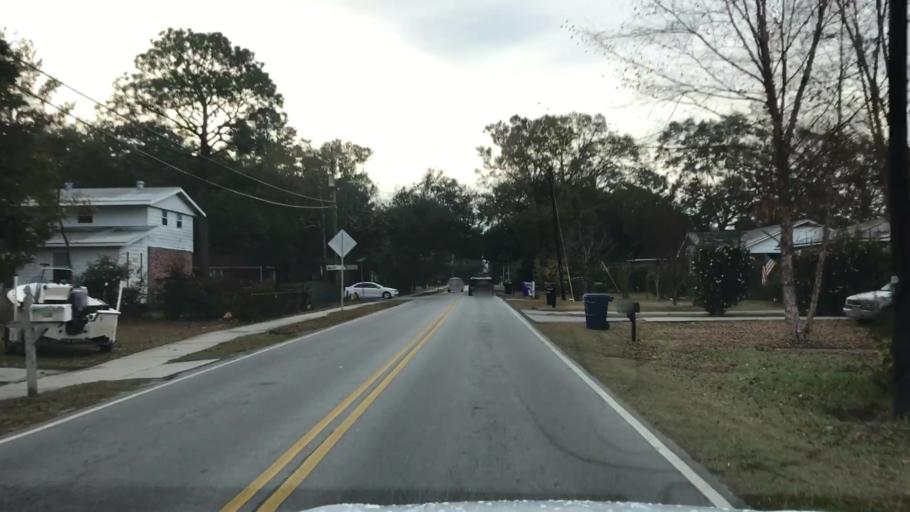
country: US
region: South Carolina
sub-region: Charleston County
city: North Charleston
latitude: 32.8051
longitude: -80.0084
